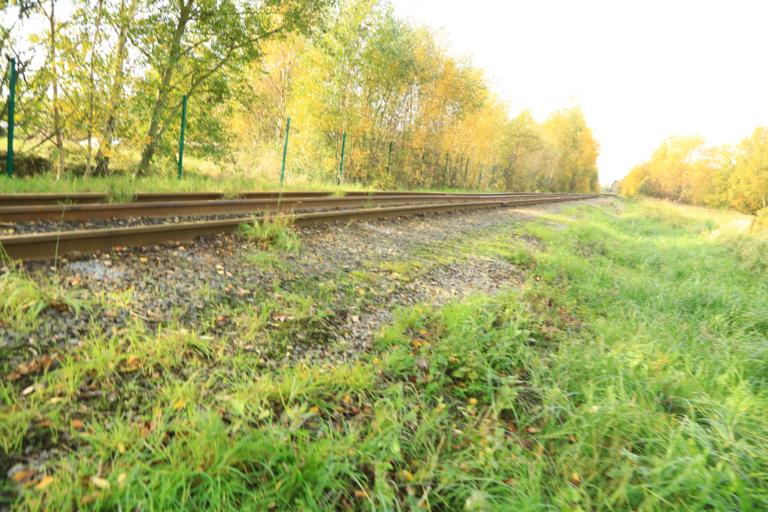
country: SE
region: Halland
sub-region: Varbergs Kommun
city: Varberg
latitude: 57.1206
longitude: 12.2492
